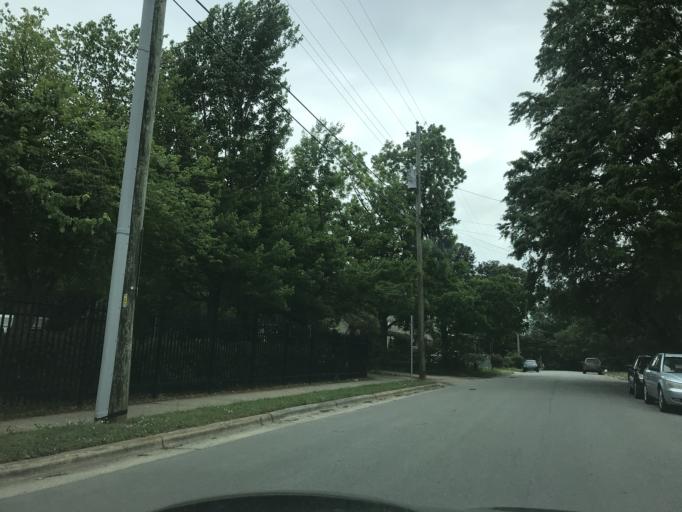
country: US
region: North Carolina
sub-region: Wake County
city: West Raleigh
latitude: 35.7901
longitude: -78.6905
